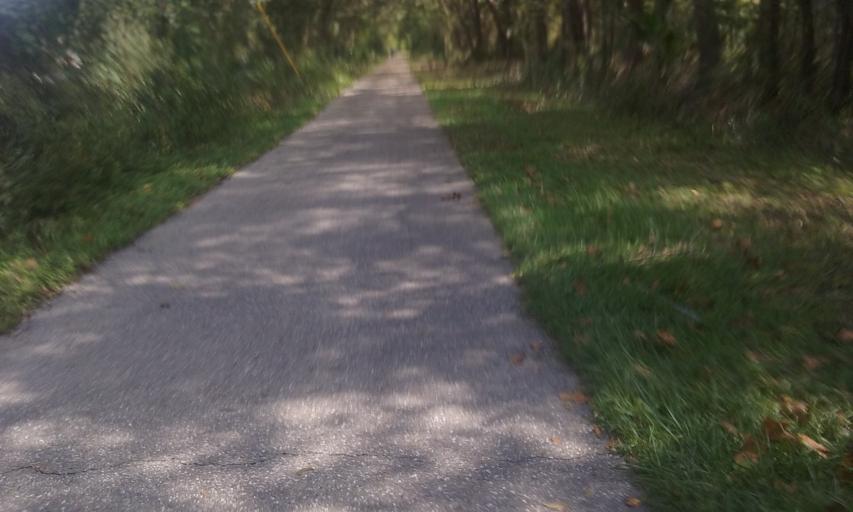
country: US
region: Florida
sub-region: Alachua County
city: Hawthorne
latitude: 29.5875
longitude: -82.0916
